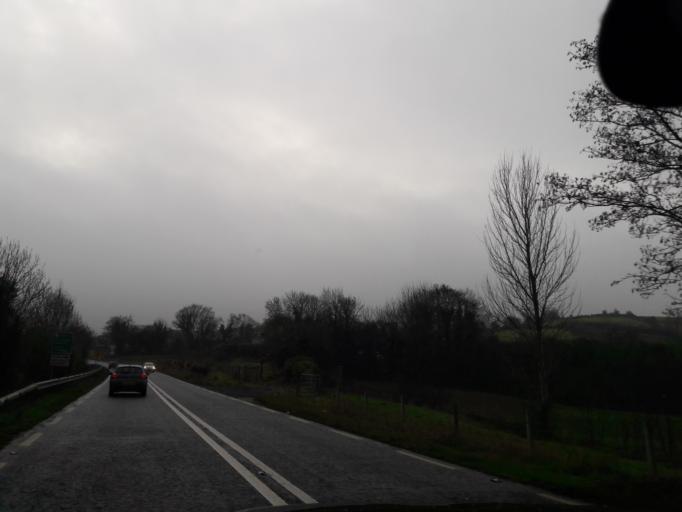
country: IE
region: Ulster
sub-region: County Donegal
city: Leifear
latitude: 54.8435
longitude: -7.4986
